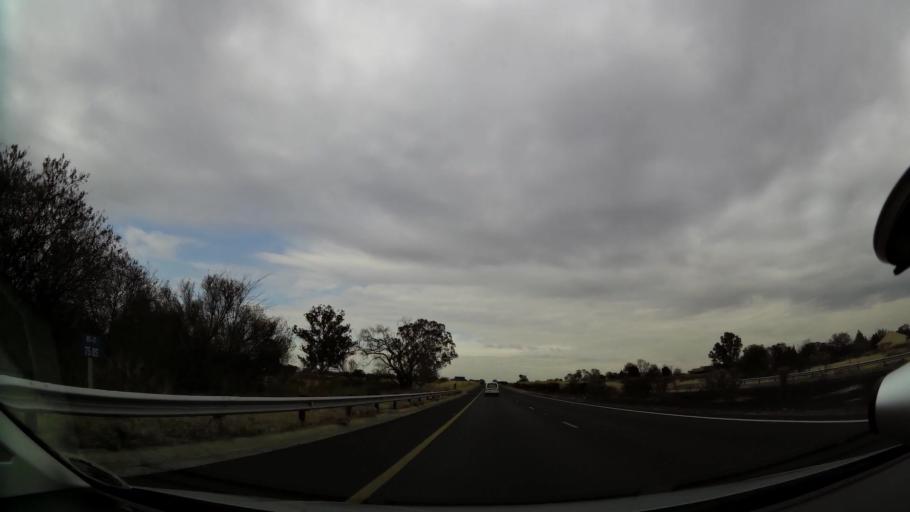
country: ZA
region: Orange Free State
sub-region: Fezile Dabi District Municipality
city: Kroonstad
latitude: -27.6341
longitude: 27.2495
